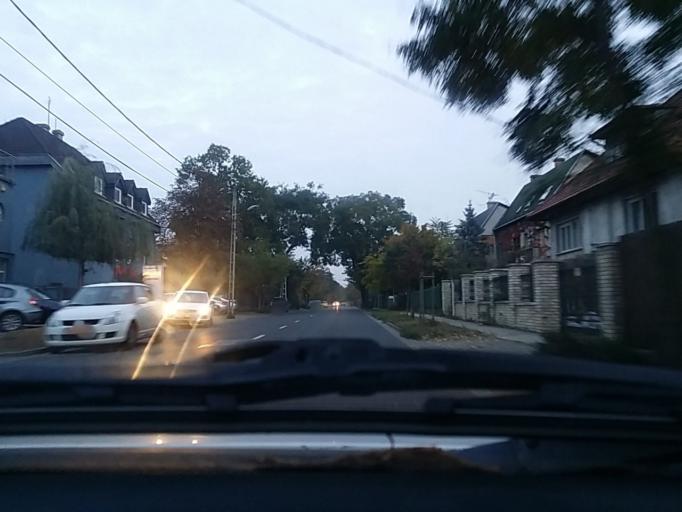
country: HU
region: Budapest
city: Budapest XIV. keruelet
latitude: 47.5340
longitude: 19.1139
